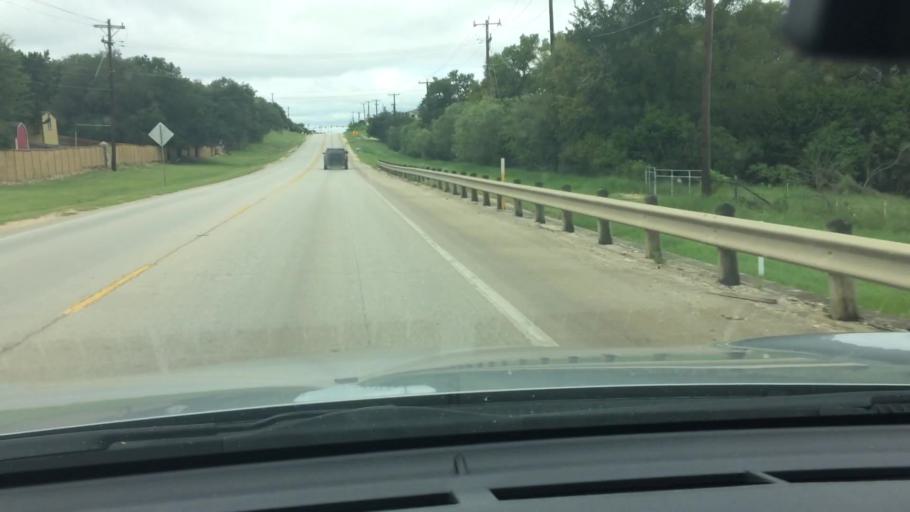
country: US
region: Texas
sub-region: Comal County
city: Garden Ridge
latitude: 29.6441
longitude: -98.3964
